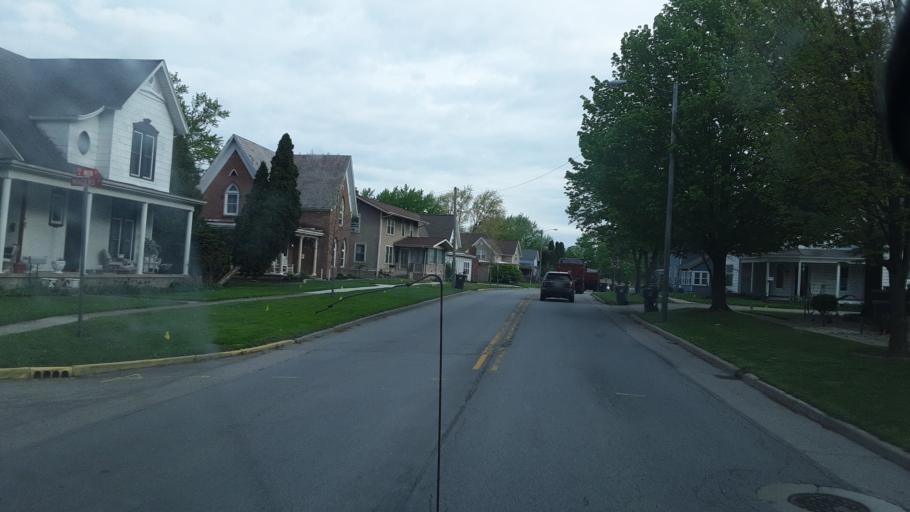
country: US
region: Indiana
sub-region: Whitley County
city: Churubusco
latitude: 41.2337
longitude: -85.3217
